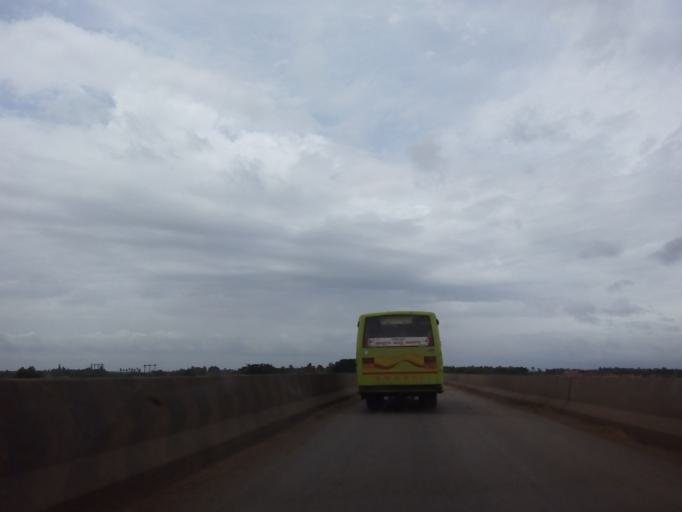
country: IN
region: Karnataka
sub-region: Davanagere
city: Harihar
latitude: 14.5135
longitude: 75.7847
